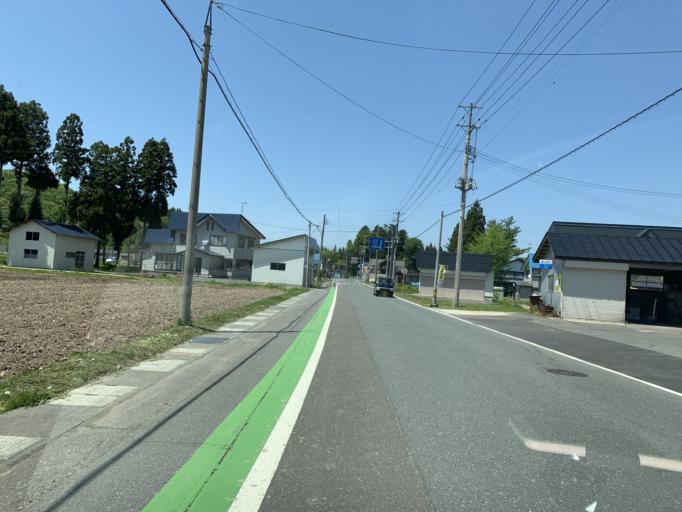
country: JP
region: Akita
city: Yokotemachi
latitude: 39.3525
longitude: 140.7692
